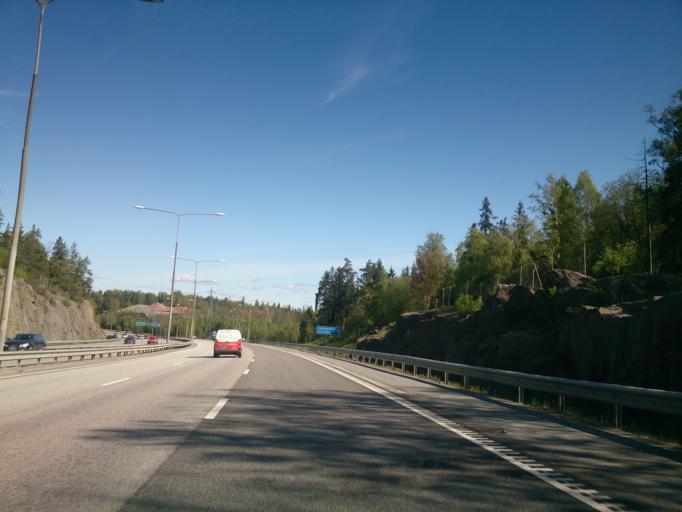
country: SE
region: Stockholm
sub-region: Haninge Kommun
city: Handen
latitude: 59.2156
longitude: 18.1347
